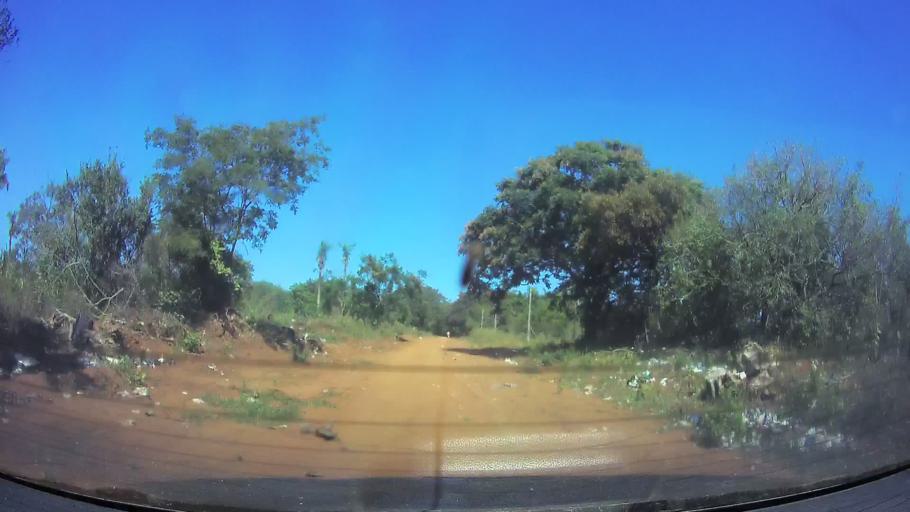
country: PY
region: Central
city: Limpio
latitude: -25.2405
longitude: -57.4531
